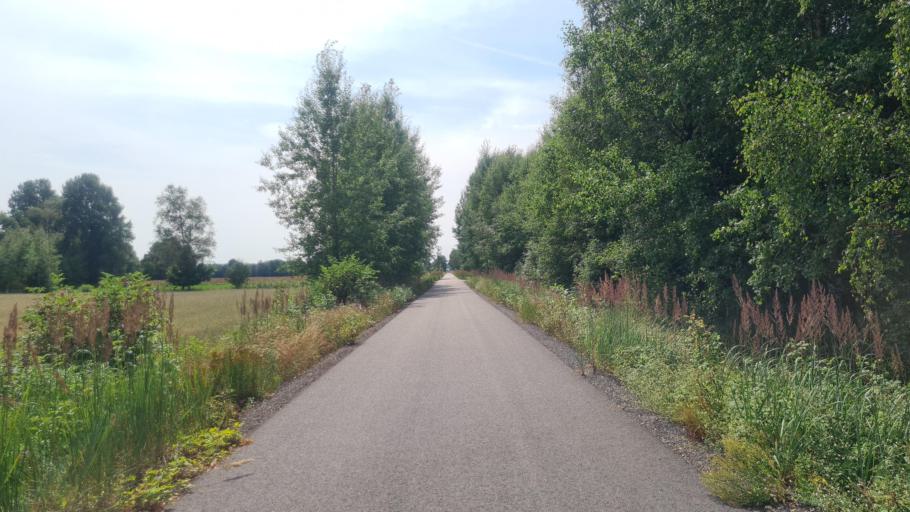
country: SE
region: Kronoberg
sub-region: Ljungby Kommun
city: Lagan
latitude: 56.8899
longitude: 13.9847
